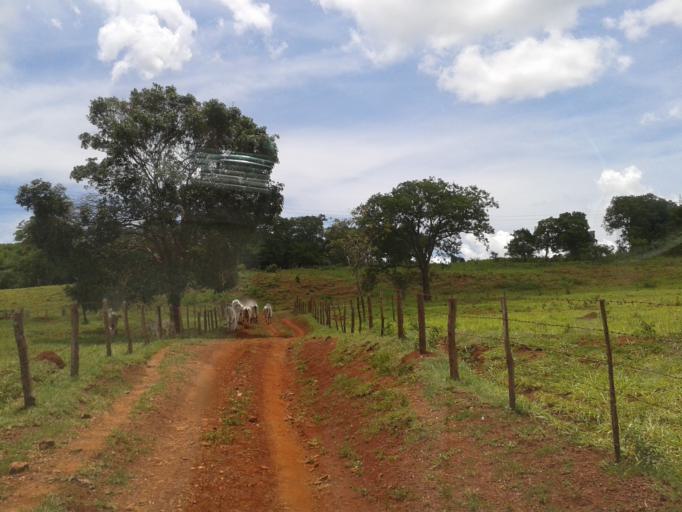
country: BR
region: Minas Gerais
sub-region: Centralina
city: Centralina
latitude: -18.6976
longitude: -49.2324
